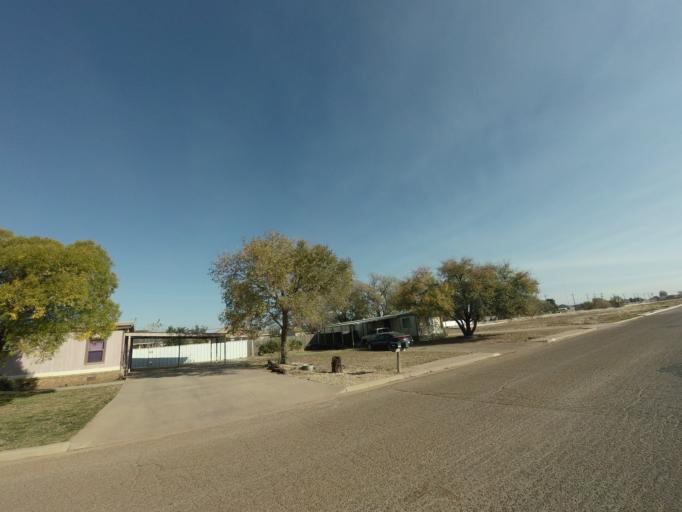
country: US
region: New Mexico
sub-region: Curry County
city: Clovis
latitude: 34.4120
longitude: -103.1752
